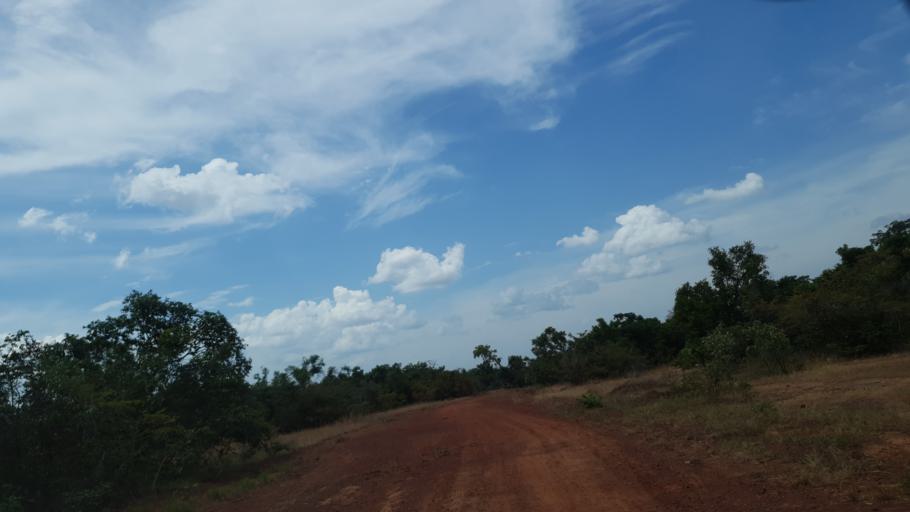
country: ML
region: Sikasso
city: Sikasso
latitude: 11.6863
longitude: -6.2164
